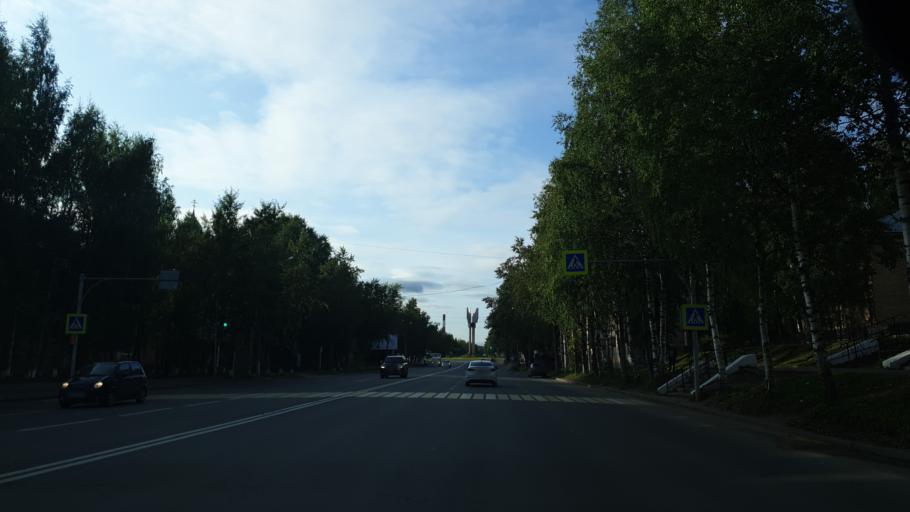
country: RU
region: Komi Republic
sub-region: Syktyvdinskiy Rayon
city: Syktyvkar
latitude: 61.6614
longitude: 50.8186
